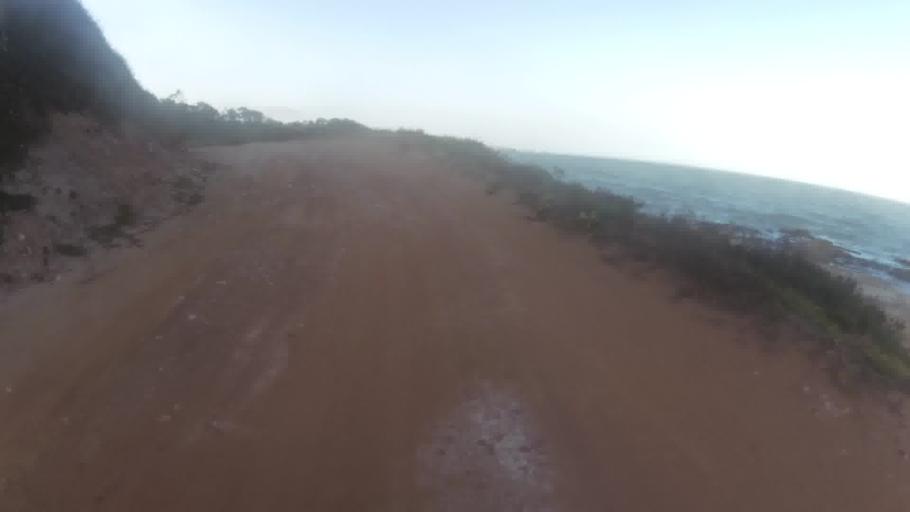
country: BR
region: Espirito Santo
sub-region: Piuma
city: Piuma
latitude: -20.8850
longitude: -40.7630
